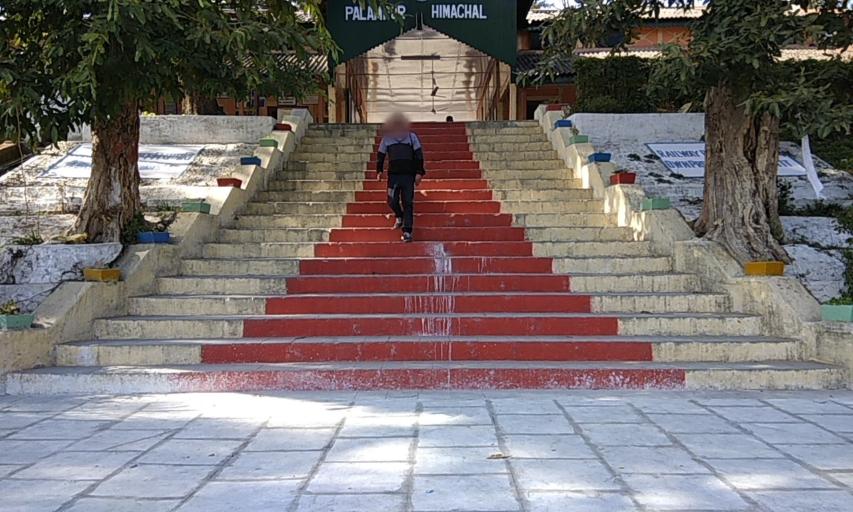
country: IN
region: Himachal Pradesh
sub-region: Kangra
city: Palampur
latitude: 32.0815
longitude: 76.5157
